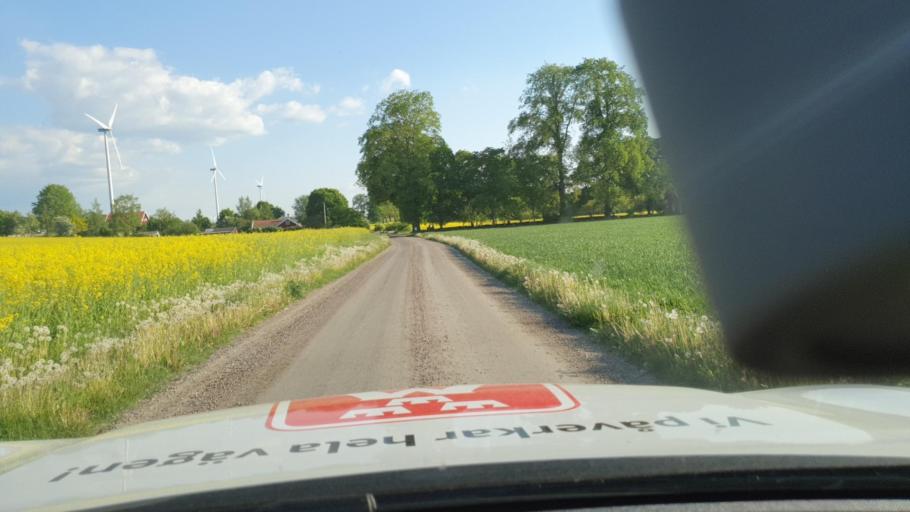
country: SE
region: Vaestra Goetaland
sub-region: Falkopings Kommun
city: Akarp
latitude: 58.1569
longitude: 13.7054
